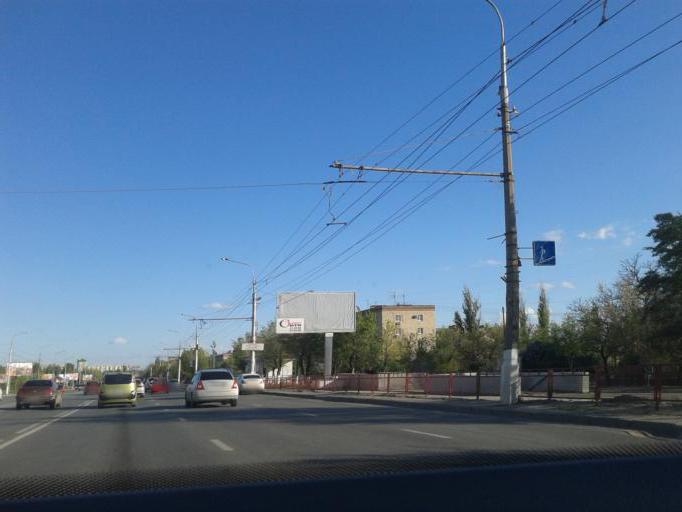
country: RU
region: Volgograd
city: Volgograd
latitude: 48.7493
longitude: 44.4854
